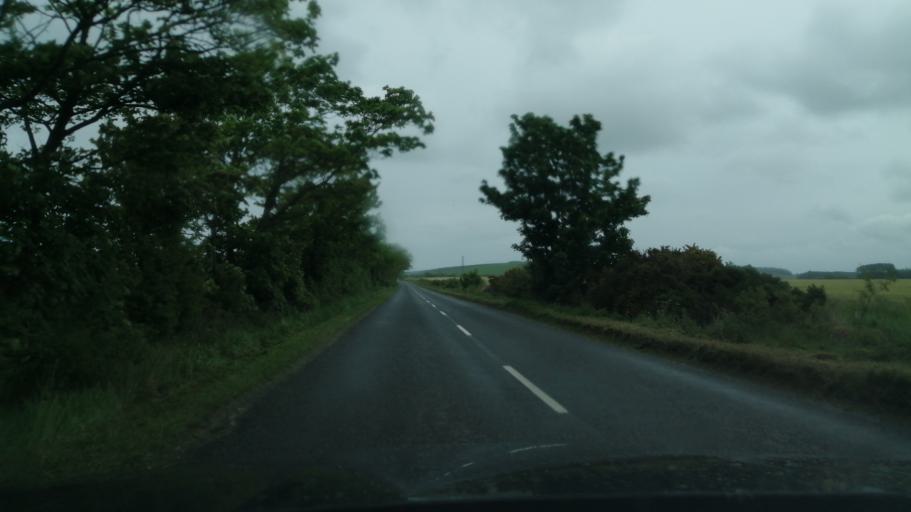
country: GB
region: Scotland
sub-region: Aberdeenshire
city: Portsoy
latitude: 57.6633
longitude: -2.6952
